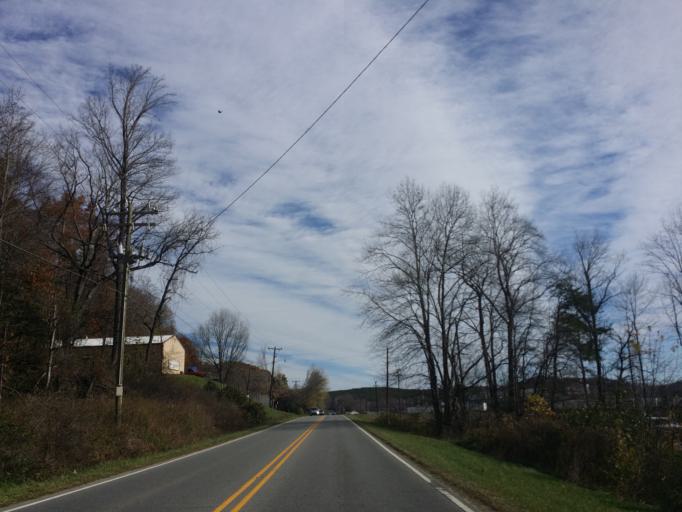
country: US
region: North Carolina
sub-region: McDowell County
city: West Marion
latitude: 35.6385
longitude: -82.1691
